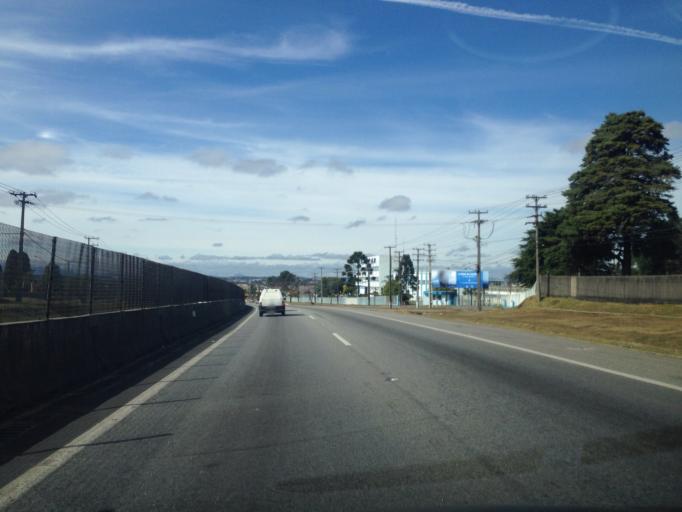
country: BR
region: Parana
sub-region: Pinhais
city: Pinhais
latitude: -25.4764
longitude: -49.2066
